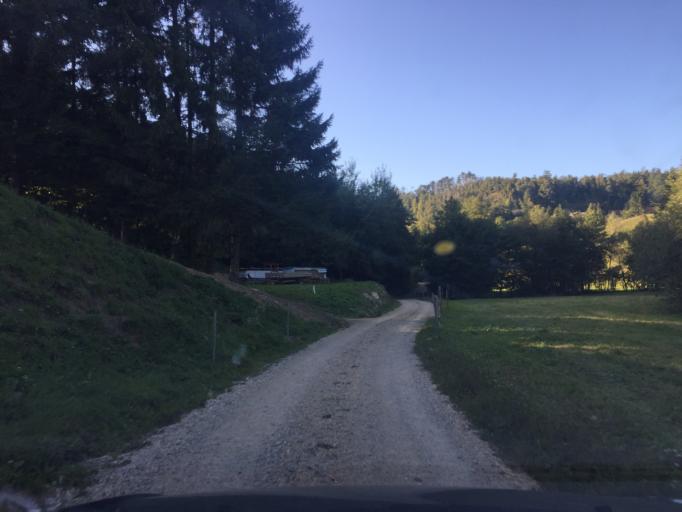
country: SI
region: Postojna
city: Postojna
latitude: 45.8104
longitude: 14.1323
